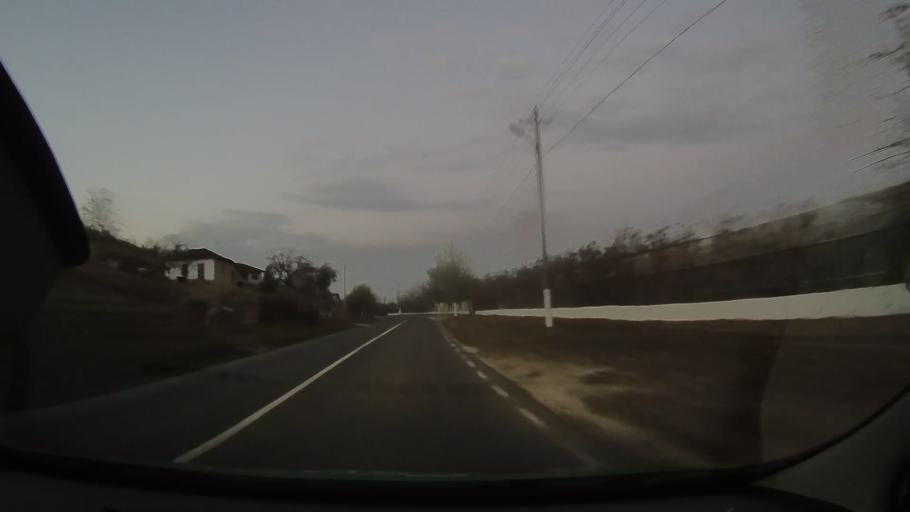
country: RO
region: Constanta
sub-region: Comuna Ion Corvin
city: Ion Corvin
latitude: 44.0980
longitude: 27.7549
